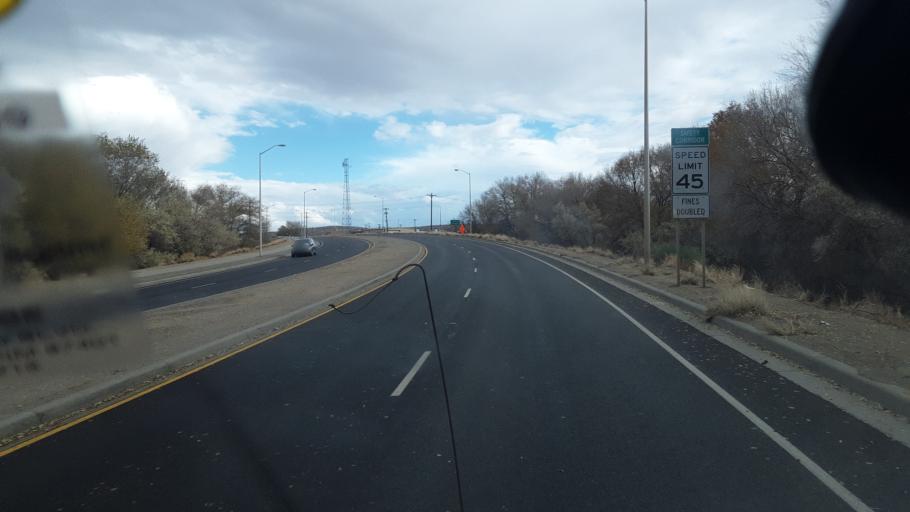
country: US
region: New Mexico
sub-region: San Juan County
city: Farmington
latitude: 36.7204
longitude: -108.2203
